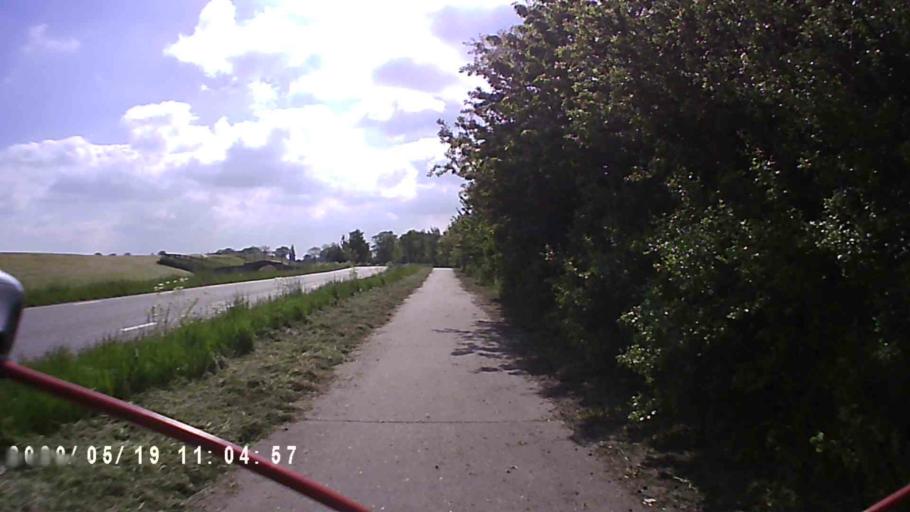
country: NL
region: Groningen
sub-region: Gemeente Zuidhorn
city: Grijpskerk
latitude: 53.2960
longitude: 6.2878
